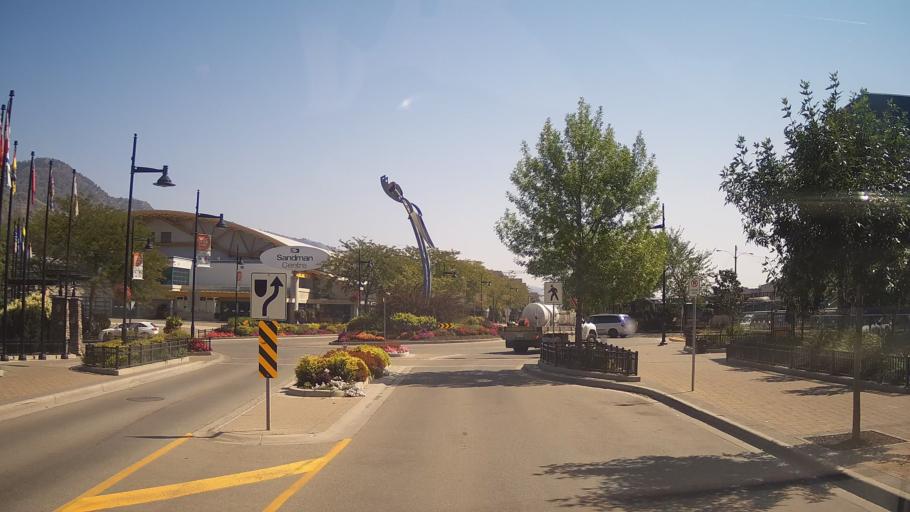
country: CA
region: British Columbia
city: Kamloops
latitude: 50.6780
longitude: -120.3351
